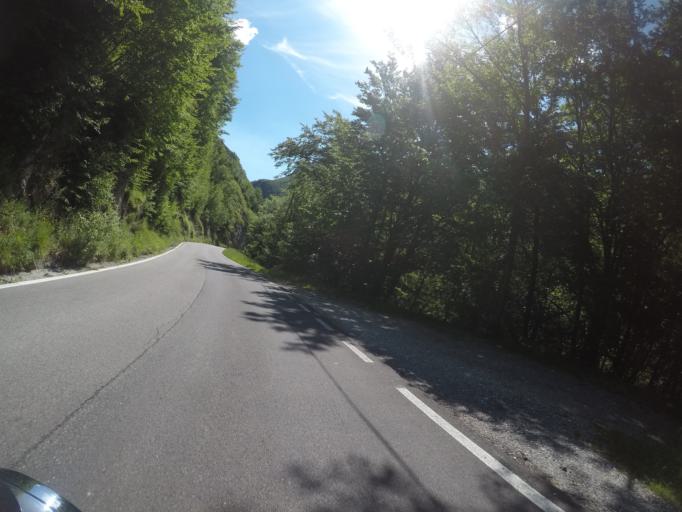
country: IT
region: Tuscany
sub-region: Provincia di Lucca
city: Fontana delle Monache
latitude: 44.0582
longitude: 10.2603
